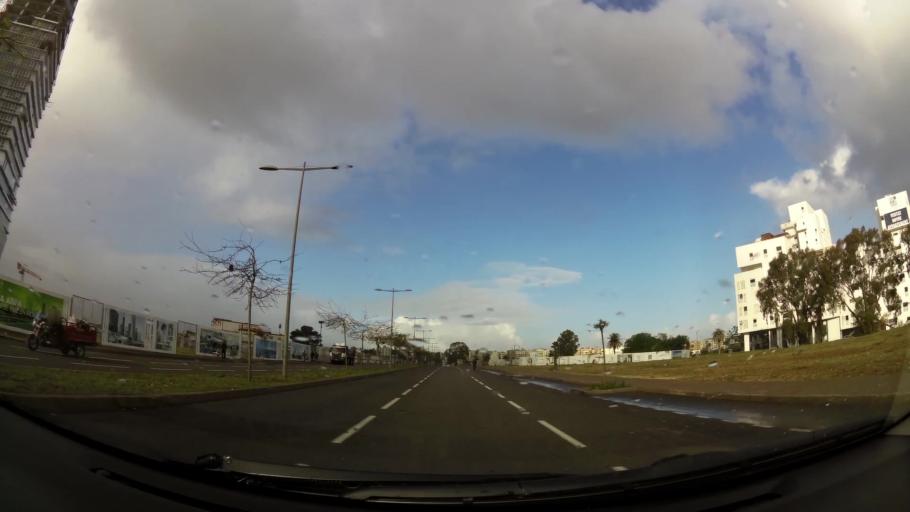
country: MA
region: Grand Casablanca
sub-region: Casablanca
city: Casablanca
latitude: 33.5648
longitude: -7.6609
